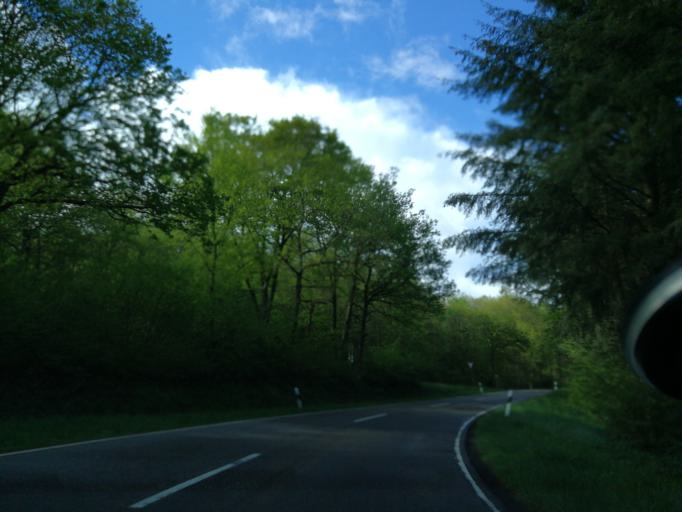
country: DE
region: Rheinland-Pfalz
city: Wittlich
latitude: 50.0048
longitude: 6.8963
